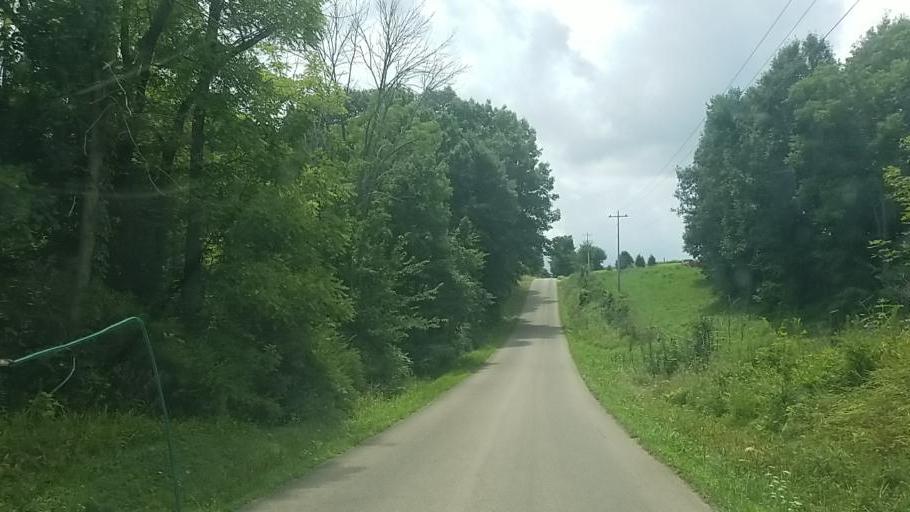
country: US
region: Ohio
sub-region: Knox County
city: Oak Hill
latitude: 40.2913
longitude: -82.2424
